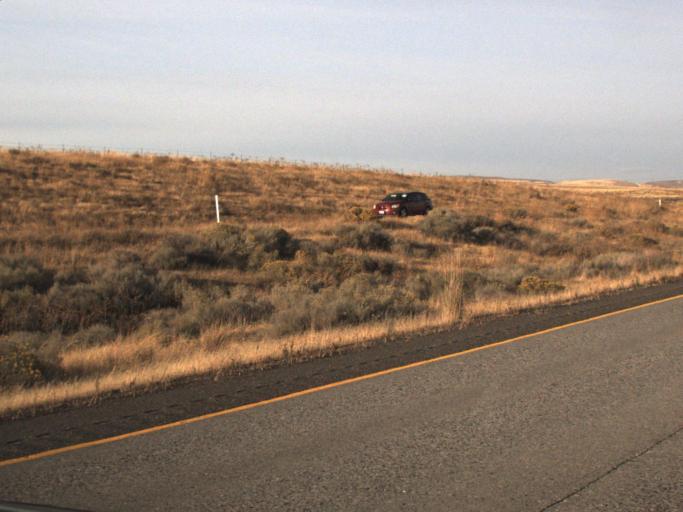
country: US
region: Oregon
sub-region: Umatilla County
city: Umatilla
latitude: 46.0127
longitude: -119.2312
